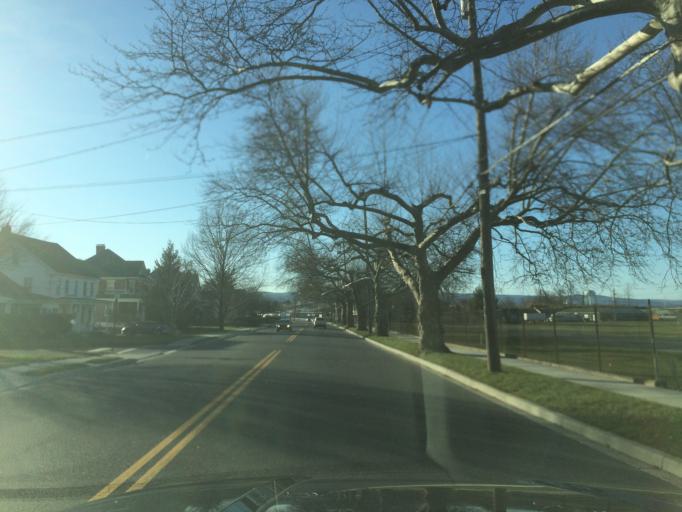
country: US
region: Maryland
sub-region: Frederick County
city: Frederick
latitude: 39.4118
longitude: -77.3965
